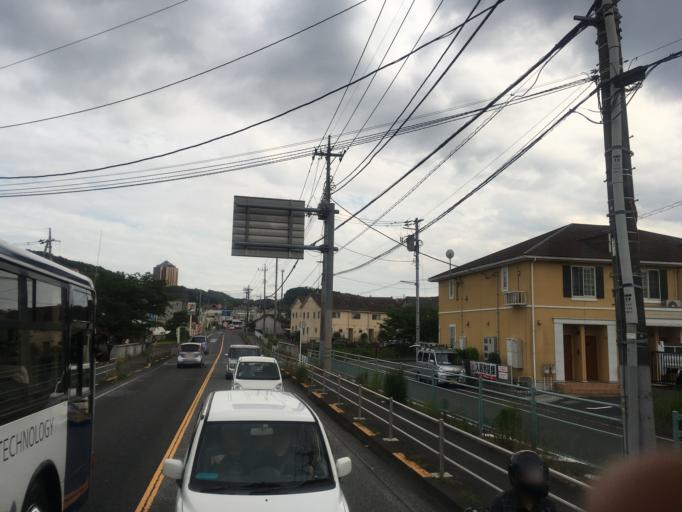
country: JP
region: Tokyo
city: Hachioji
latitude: 35.6382
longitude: 139.3395
